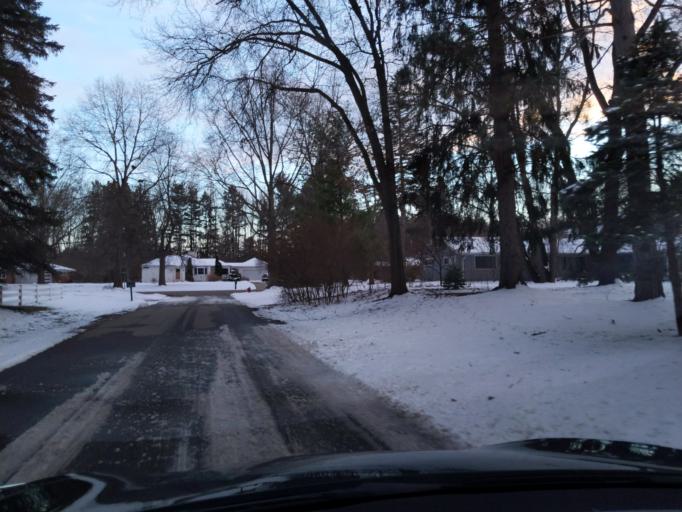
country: US
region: Michigan
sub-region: Ingham County
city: Okemos
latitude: 42.7168
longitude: -84.4416
